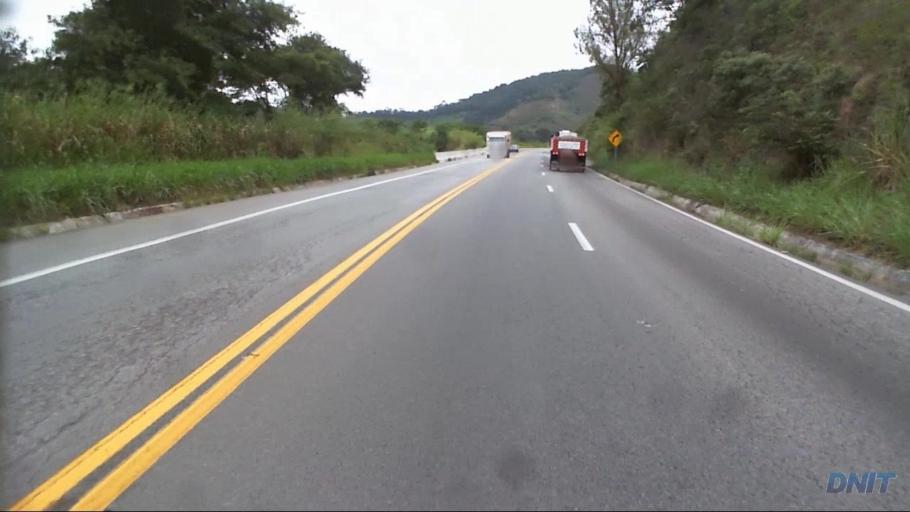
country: BR
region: Minas Gerais
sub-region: Nova Era
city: Nova Era
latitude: -19.6326
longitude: -42.8882
